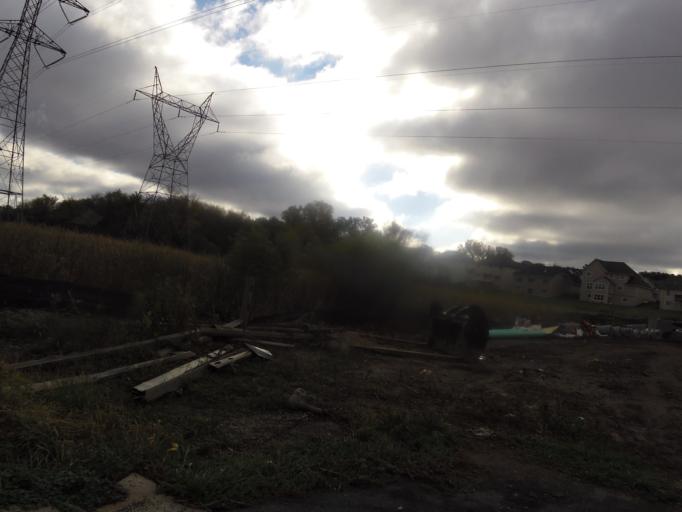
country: US
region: Minnesota
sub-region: Scott County
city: Savage
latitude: 44.7720
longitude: -93.3290
